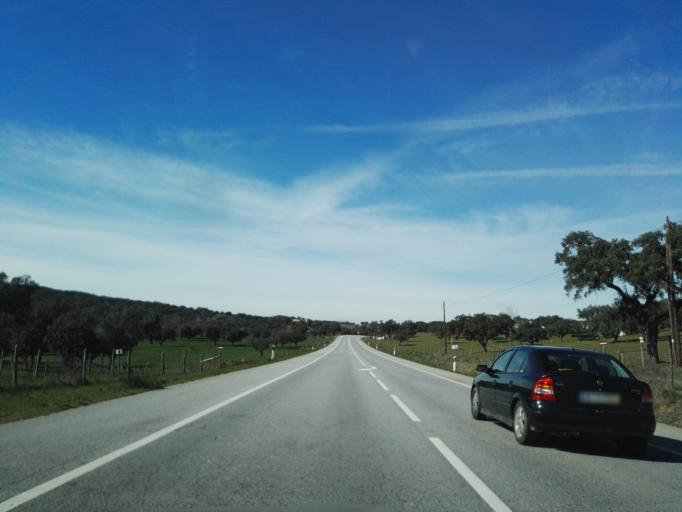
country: PT
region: Portalegre
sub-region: Portalegre
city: Alegrete
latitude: 39.1893
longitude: -7.3538
